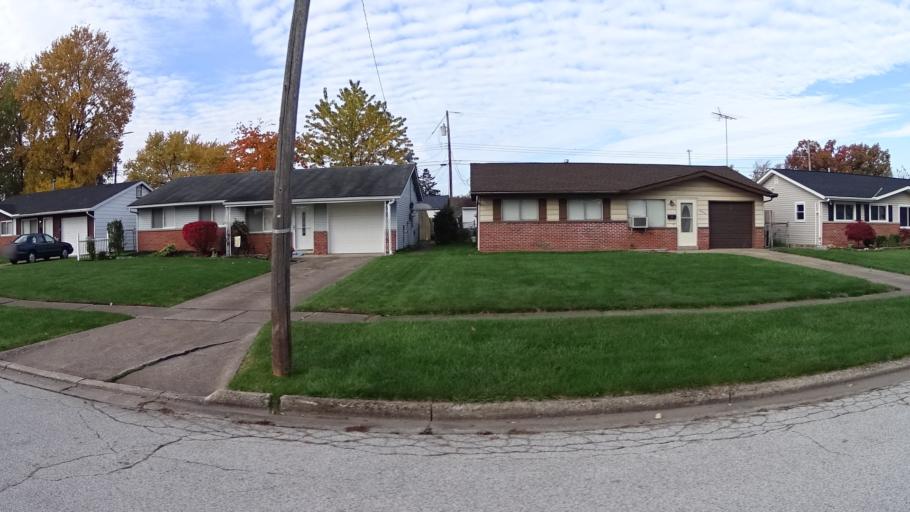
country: US
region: Ohio
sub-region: Lorain County
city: Sheffield
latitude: 41.4257
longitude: -82.1151
